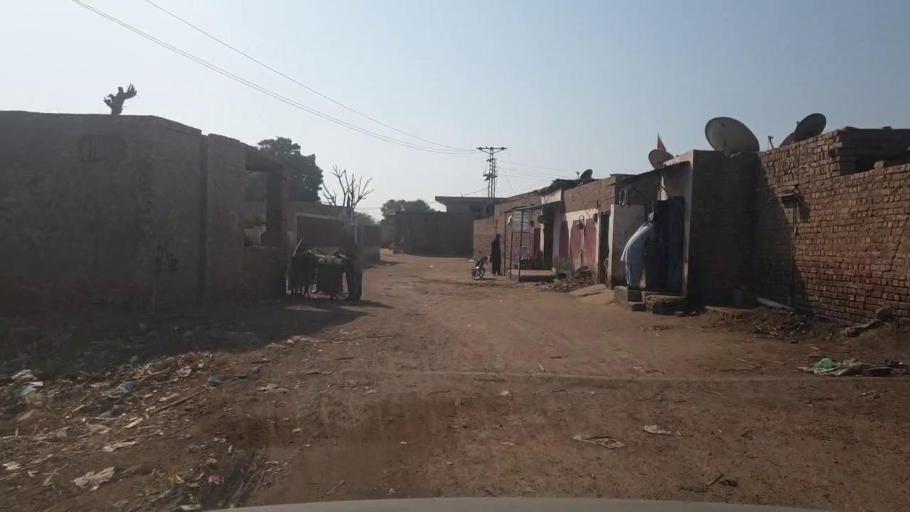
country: PK
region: Sindh
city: Tando Allahyar
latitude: 25.4674
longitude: 68.7438
